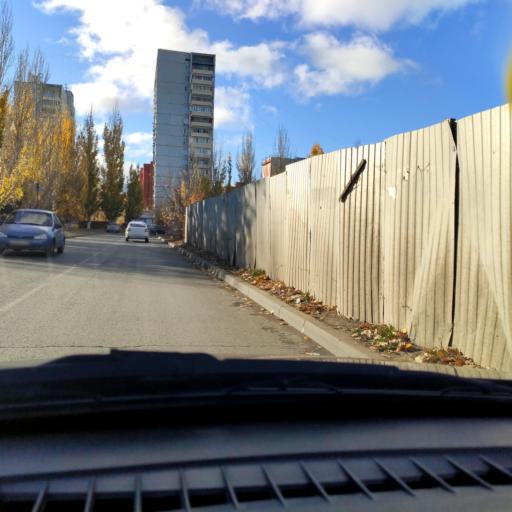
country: RU
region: Samara
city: Tol'yatti
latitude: 53.5377
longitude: 49.3379
